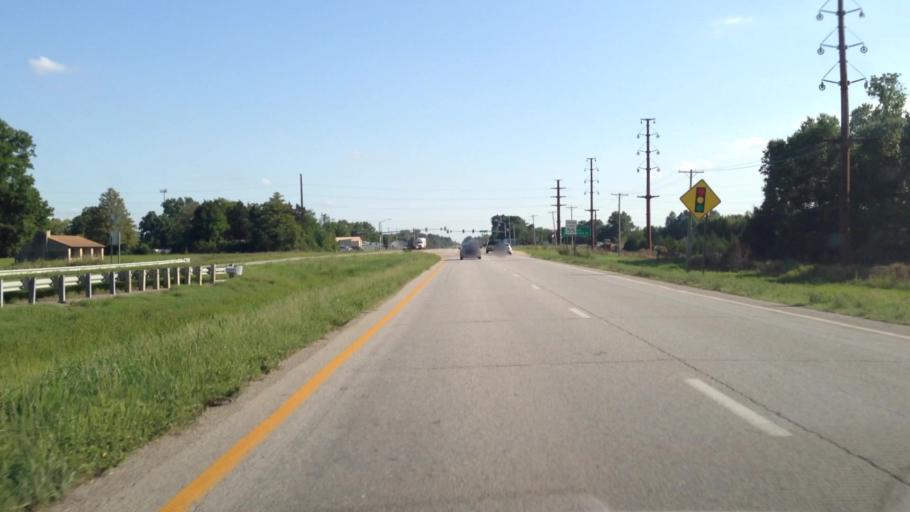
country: US
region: Kansas
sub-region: Crawford County
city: Frontenac
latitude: 37.4726
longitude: -94.7053
